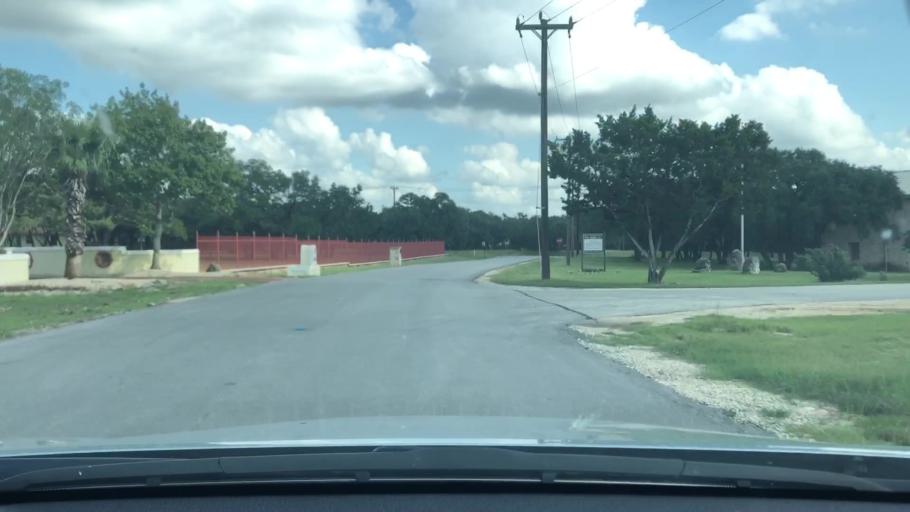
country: US
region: Texas
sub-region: Bexar County
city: Fair Oaks Ranch
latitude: 29.7555
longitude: -98.6236
